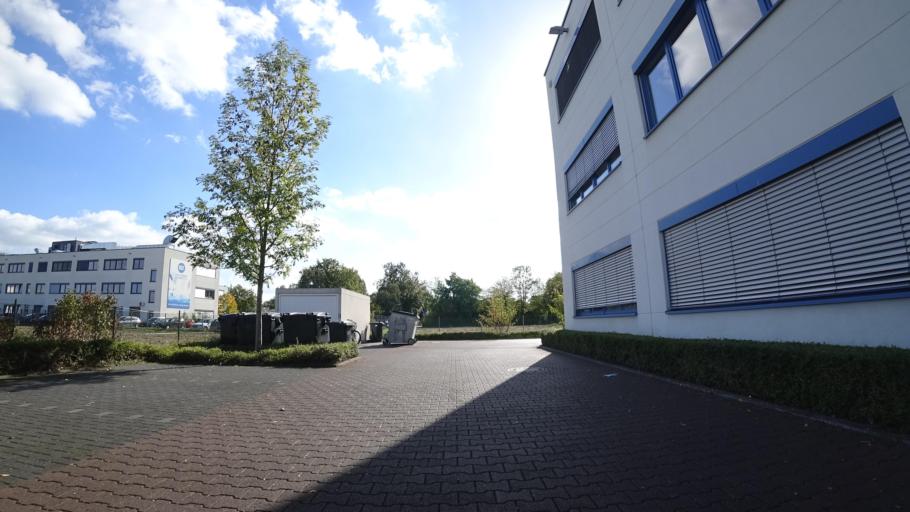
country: DE
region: North Rhine-Westphalia
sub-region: Regierungsbezirk Detmold
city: Rheda-Wiedenbruck
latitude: 51.8652
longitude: 8.2956
